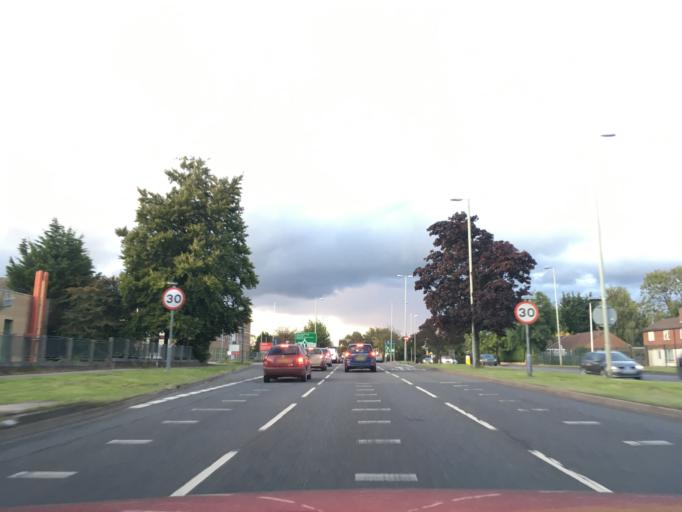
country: GB
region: England
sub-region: Gloucestershire
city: Barnwood
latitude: 51.8627
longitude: -2.2145
